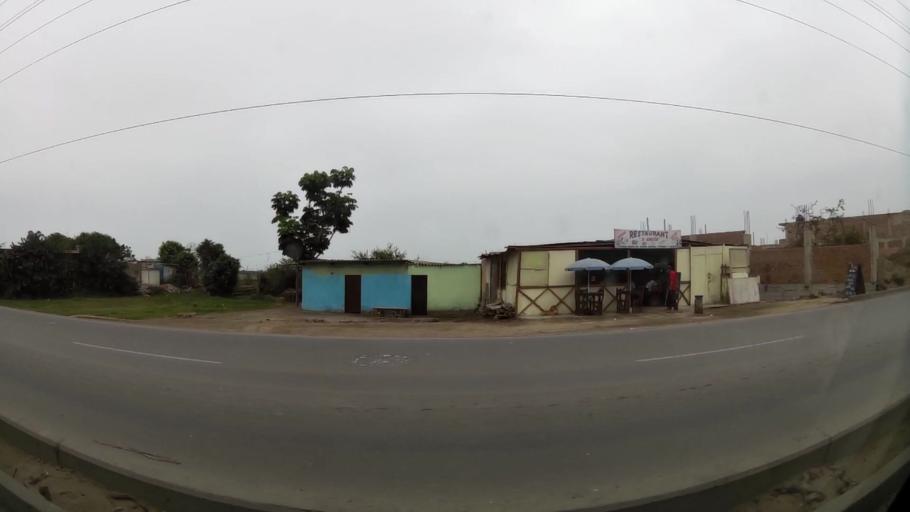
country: PE
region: Lima
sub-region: Lima
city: Punta Hermosa
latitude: -12.2803
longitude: -76.8670
